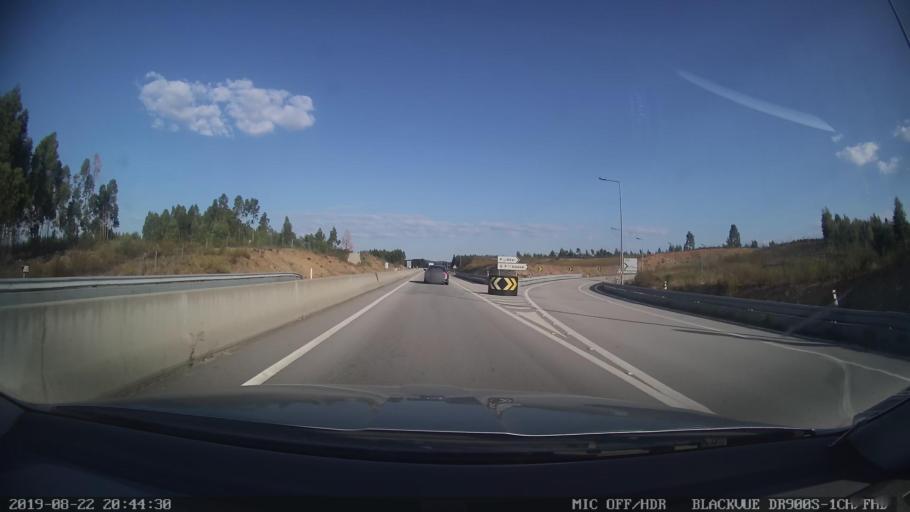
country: PT
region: Castelo Branco
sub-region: Proenca-A-Nova
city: Proenca-a-Nova
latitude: 39.7080
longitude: -7.8525
